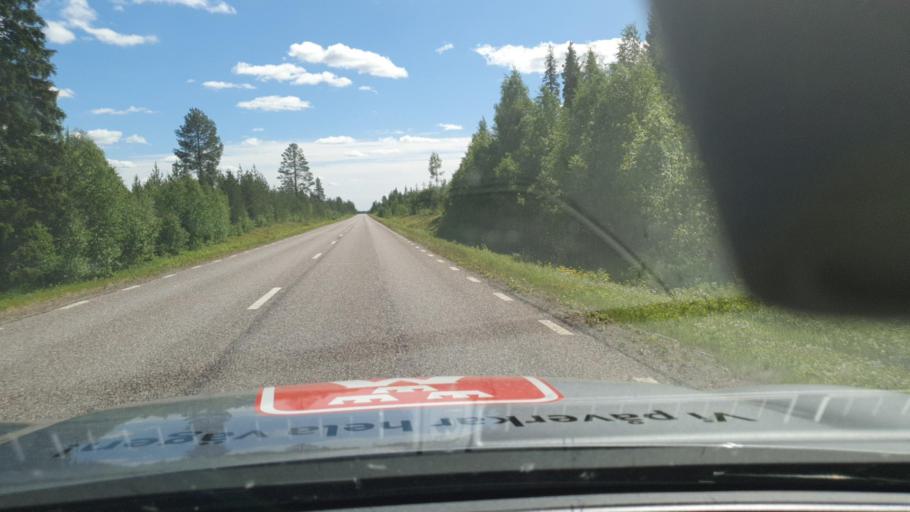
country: SE
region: Norrbotten
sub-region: Pajala Kommun
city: Pajala
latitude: 67.1561
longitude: 23.5518
